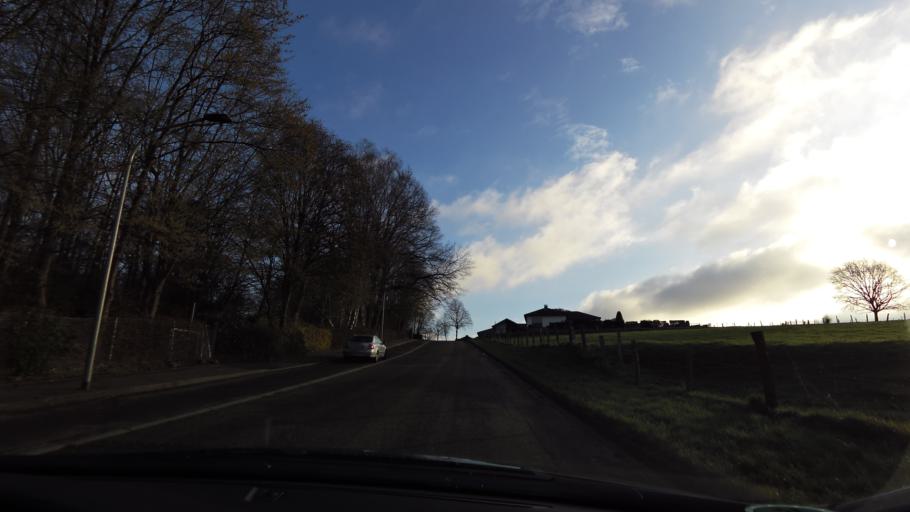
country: DE
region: North Rhine-Westphalia
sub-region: Regierungsbezirk Koln
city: Herzogenrath
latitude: 50.8789
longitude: 6.0942
